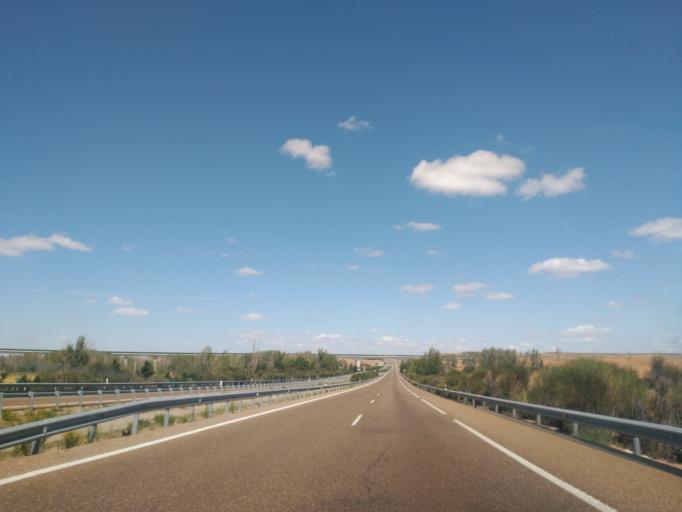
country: ES
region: Castille and Leon
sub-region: Provincia de Valladolid
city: Siete Iglesias de Trabancos
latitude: 41.3704
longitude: -5.1621
